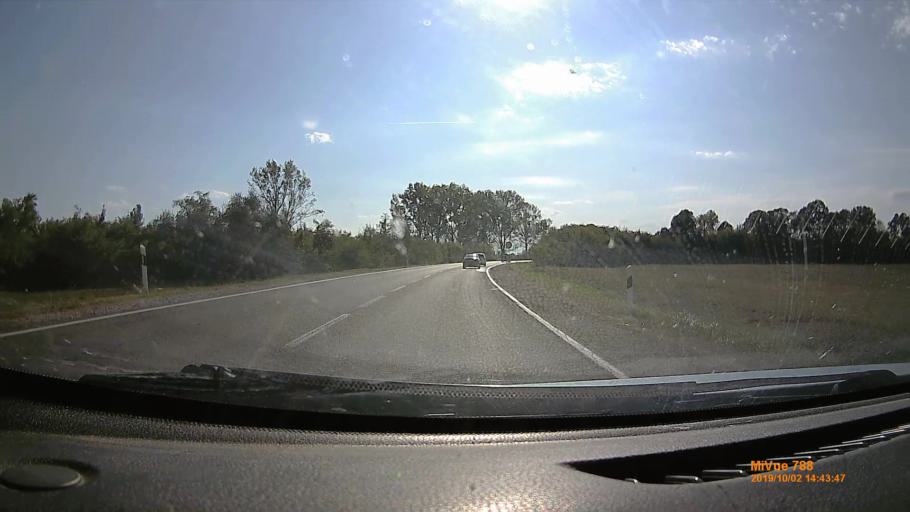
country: HU
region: Heves
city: Szihalom
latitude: 47.7714
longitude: 20.4621
